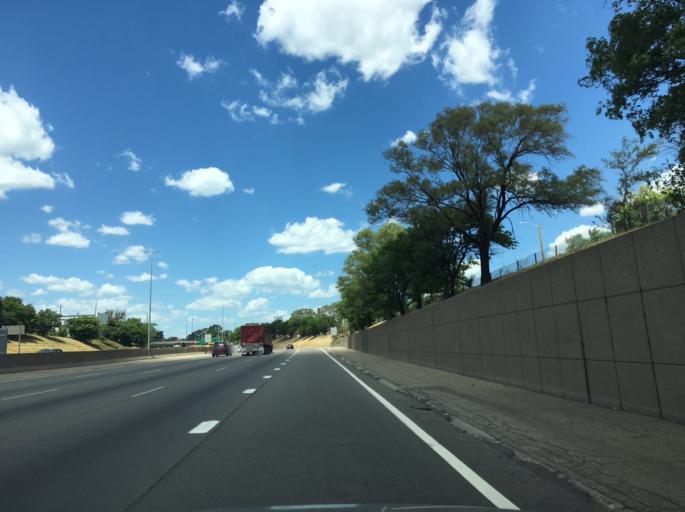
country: US
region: Michigan
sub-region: Wayne County
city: Highland Park
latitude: 42.4035
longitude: -83.0725
